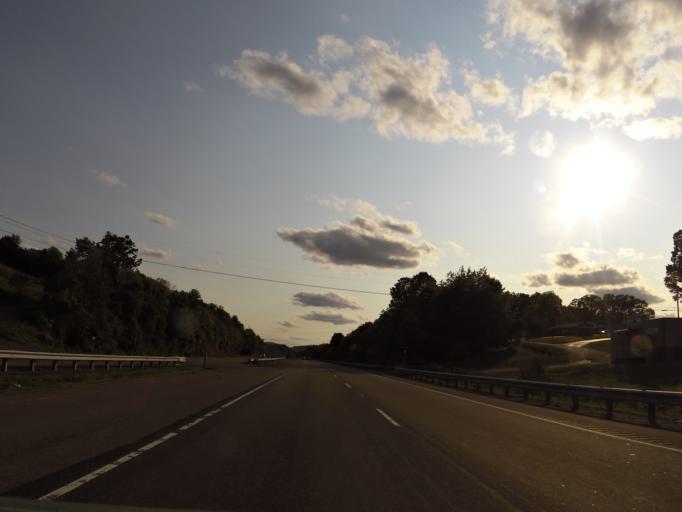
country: US
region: Virginia
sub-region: Tazewell County
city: Claypool Hill
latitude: 37.0063
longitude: -81.8029
